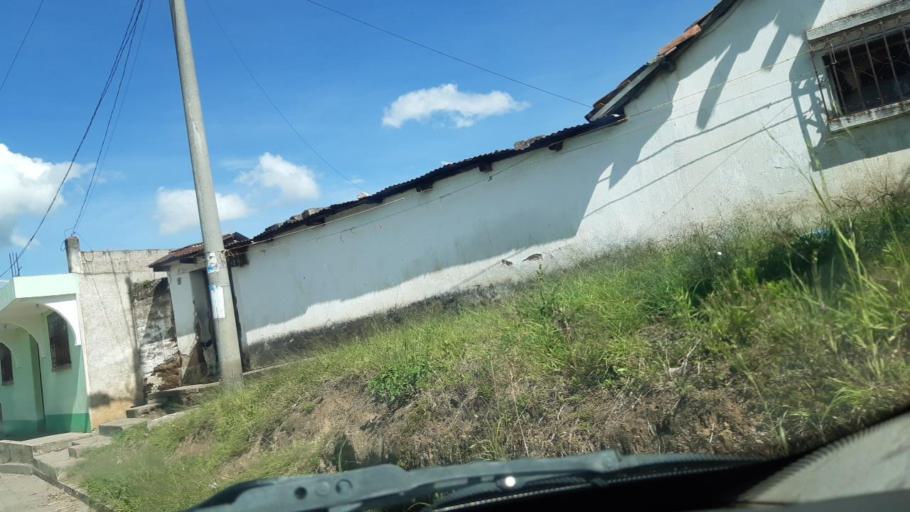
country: GT
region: Quetzaltenango
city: Salcaja
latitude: 14.8860
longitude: -91.4527
